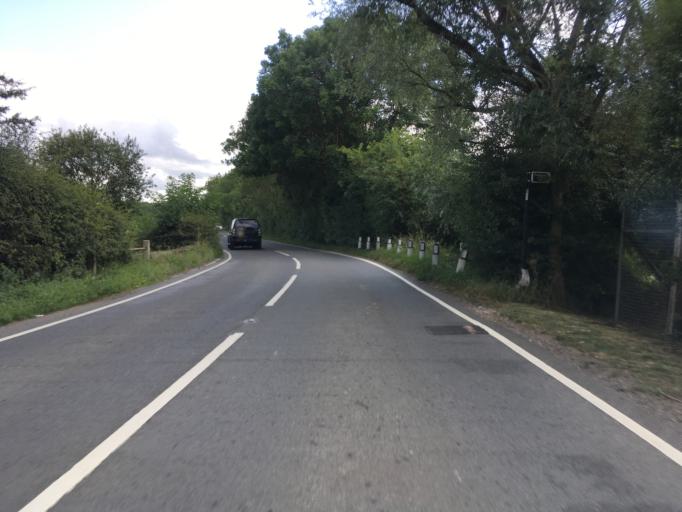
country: GB
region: England
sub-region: Kent
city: Headcorn
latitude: 51.1609
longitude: 0.6327
